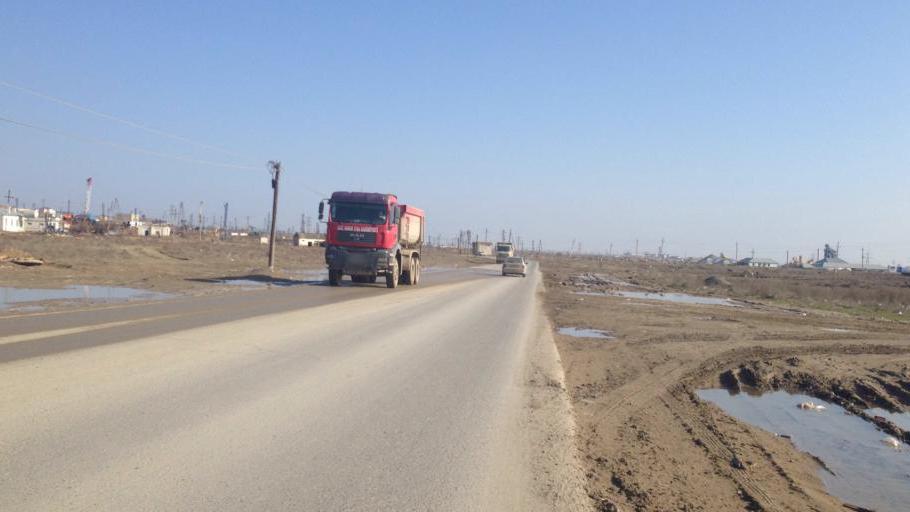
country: AZ
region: Baki
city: Balakhani
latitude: 40.4519
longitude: 49.9018
